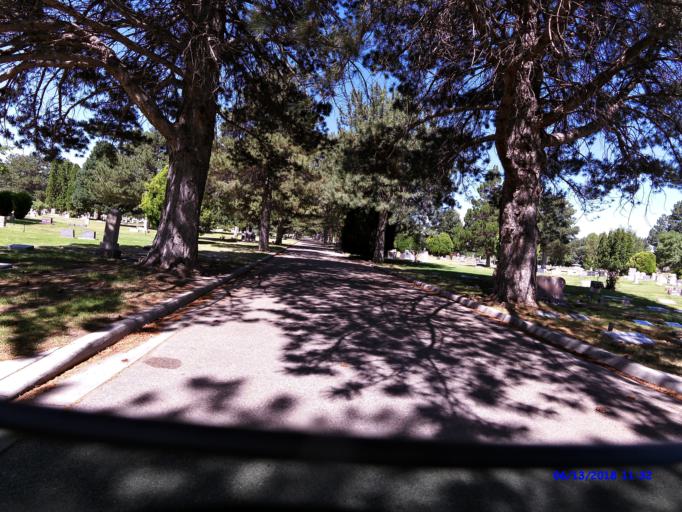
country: US
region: Utah
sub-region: Weber County
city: Ogden
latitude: 41.2325
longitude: -111.9628
